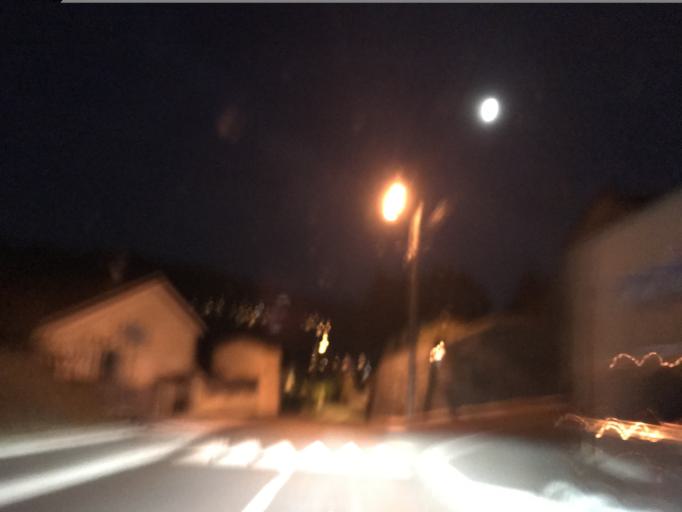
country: FR
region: Auvergne
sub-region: Departement du Puy-de-Dome
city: Thiers
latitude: 45.8576
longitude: 3.5345
